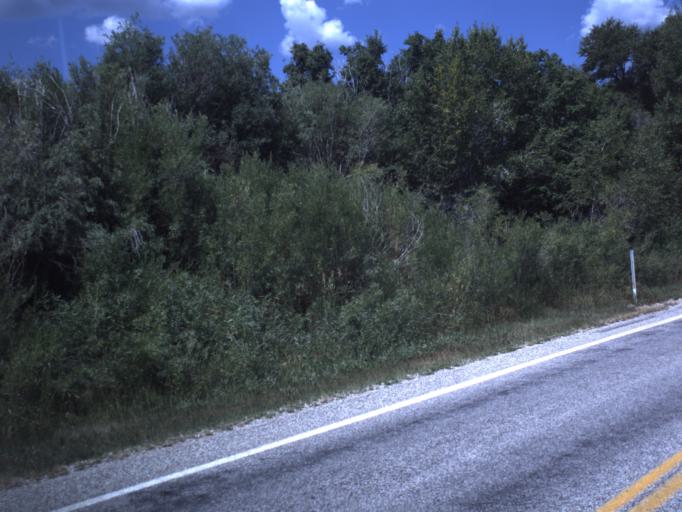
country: US
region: Idaho
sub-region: Bear Lake County
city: Paris
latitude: 41.9683
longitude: -111.4007
